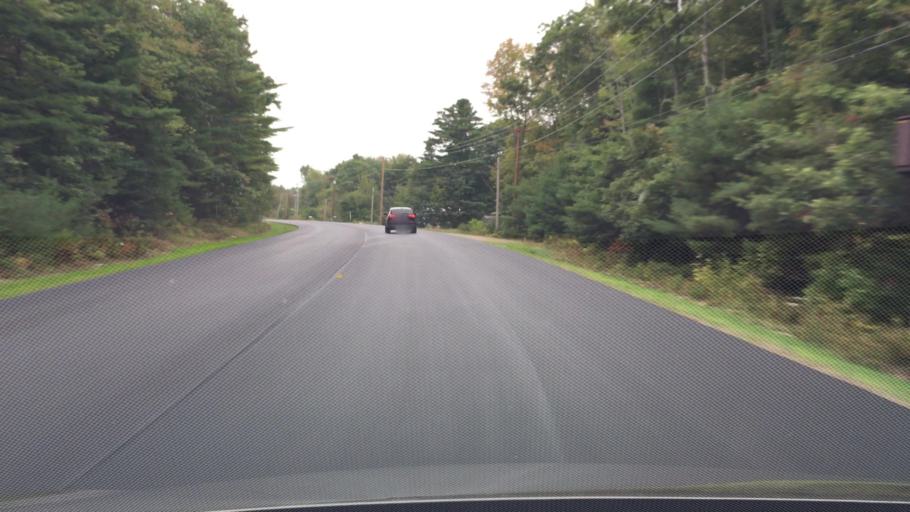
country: US
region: Maine
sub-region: Waldo County
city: Belfast
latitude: 44.4088
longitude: -69.0969
